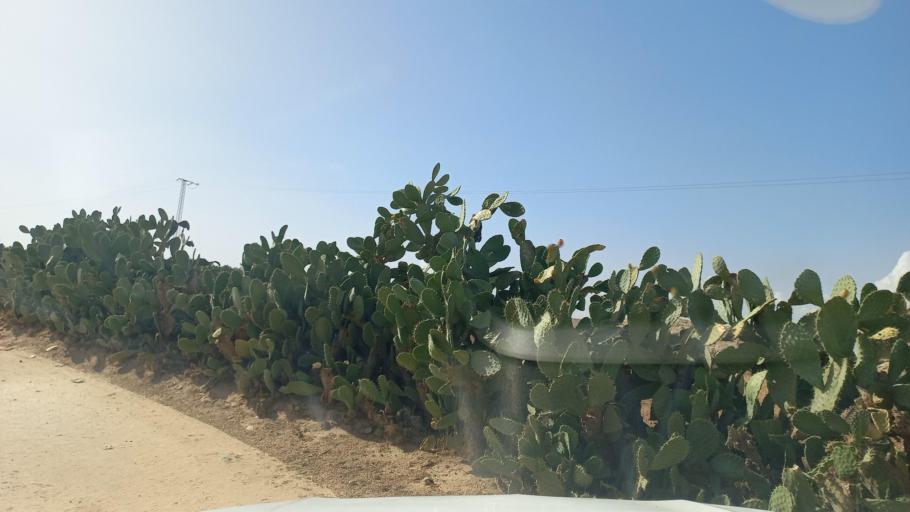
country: TN
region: Al Qasrayn
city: Sbiba
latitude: 35.3179
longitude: 9.0256
